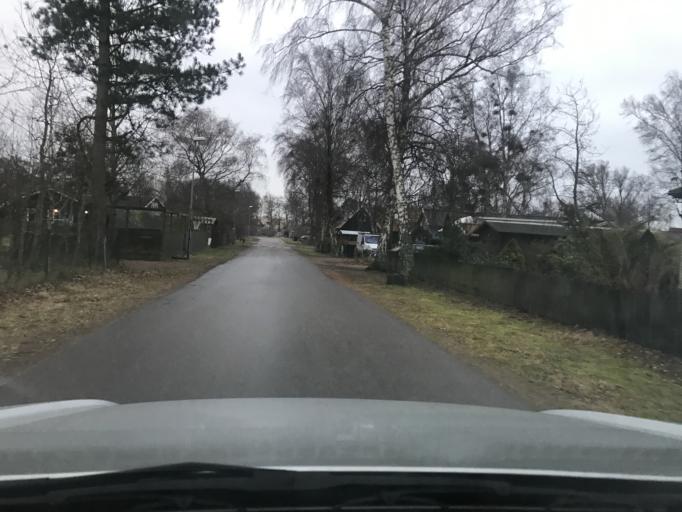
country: SE
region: Skane
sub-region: Hoganas Kommun
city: Hoganas
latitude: 56.2309
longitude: 12.5429
